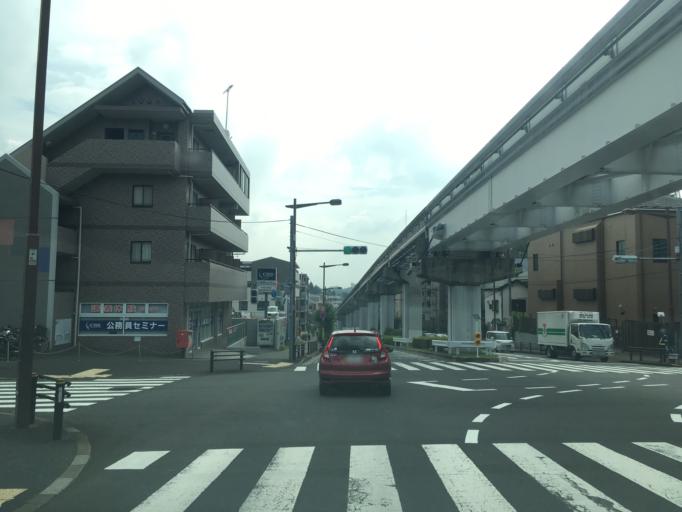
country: JP
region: Tokyo
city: Hino
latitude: 35.6416
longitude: 139.4097
